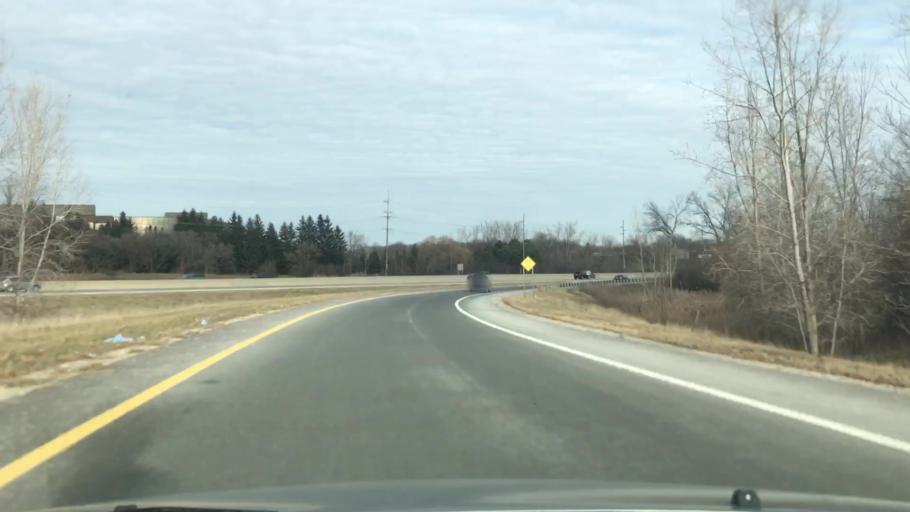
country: US
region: Michigan
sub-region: Oakland County
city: Auburn Hills
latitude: 42.6427
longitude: -83.2166
